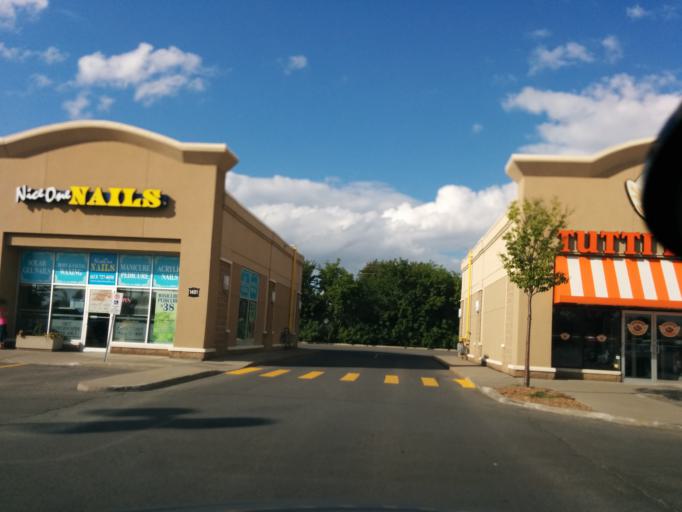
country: CA
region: Ontario
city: Ottawa
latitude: 45.3613
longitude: -75.7336
